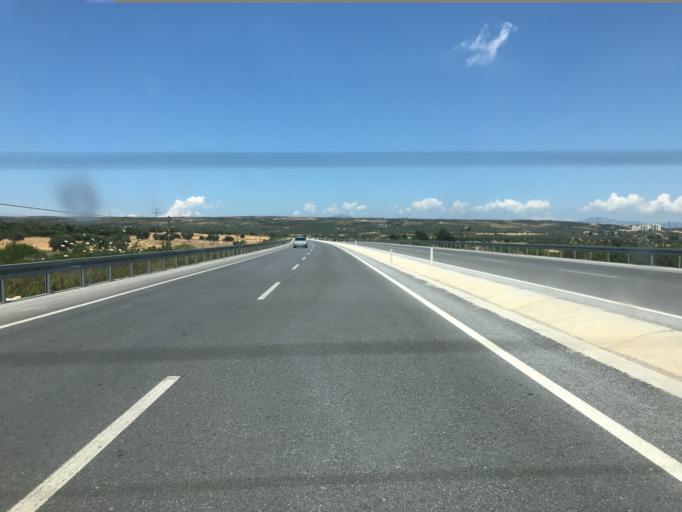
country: TR
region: Aydin
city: Akkoy
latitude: 37.4541
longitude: 27.3445
